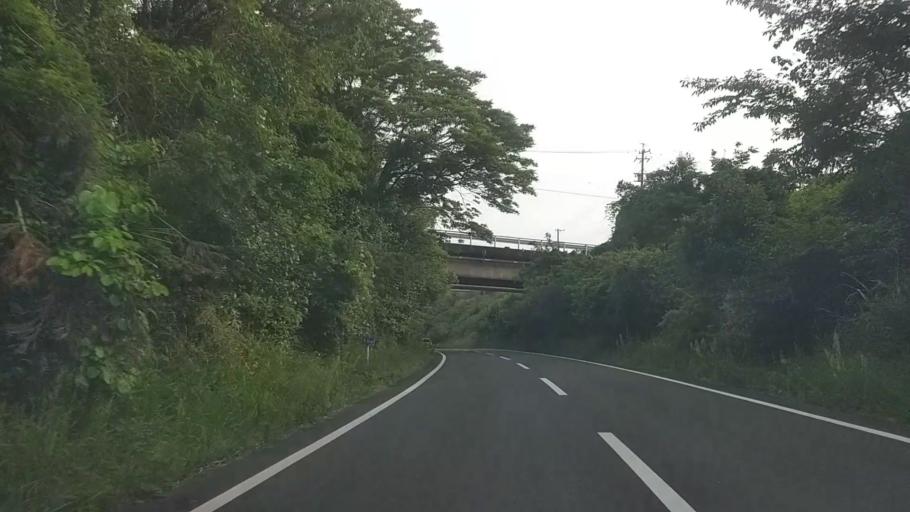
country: JP
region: Shizuoka
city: Kosai-shi
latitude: 34.7561
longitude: 137.6124
